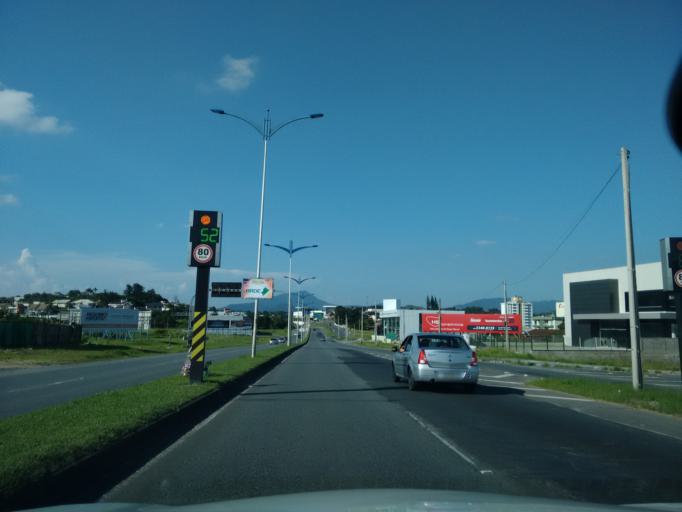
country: BR
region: Santa Catarina
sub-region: Blumenau
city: Blumenau
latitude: -26.8922
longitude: -49.0712
